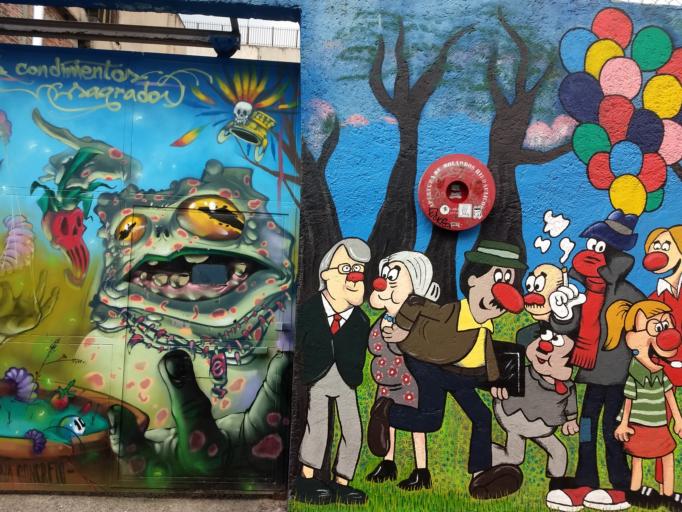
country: MX
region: Mexico City
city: Mexico City
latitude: 19.4279
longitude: -99.1366
